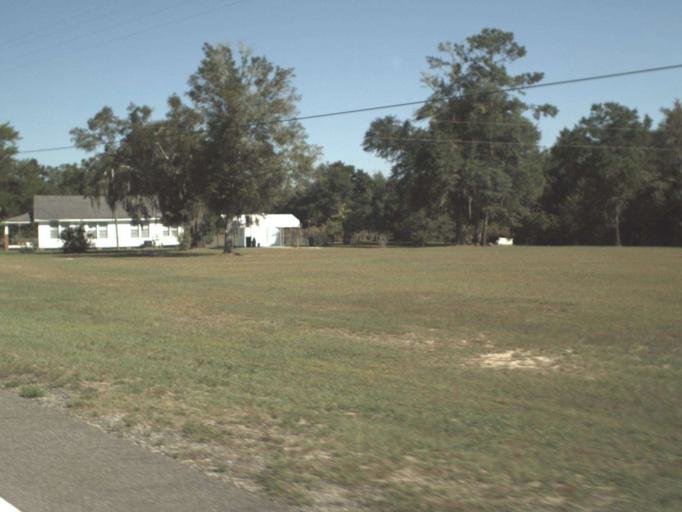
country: US
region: Florida
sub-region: Walton County
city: Freeport
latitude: 30.5640
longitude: -85.9205
